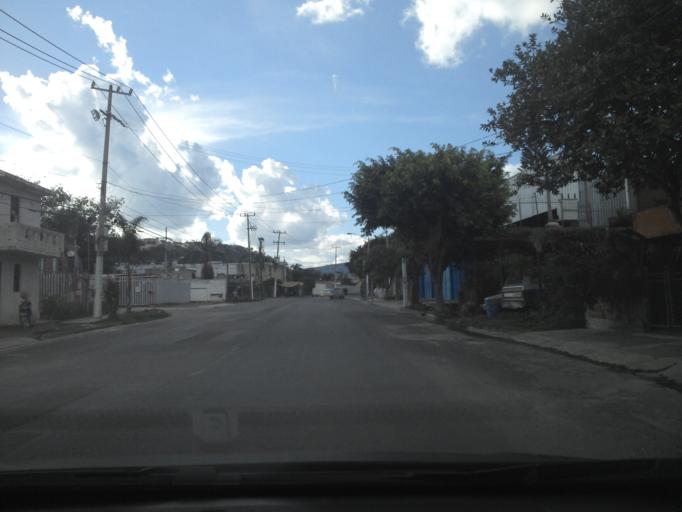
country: MX
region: Jalisco
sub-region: Tlajomulco de Zuniga
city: Palomar
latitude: 20.6177
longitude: -103.4507
